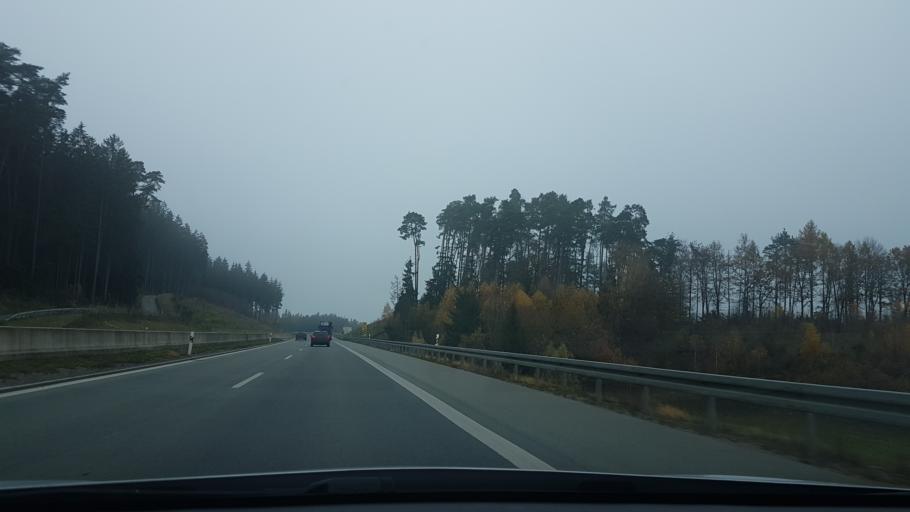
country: DE
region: Bavaria
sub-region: Lower Bavaria
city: Ergoldsbach
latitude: 48.7096
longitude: 12.1741
